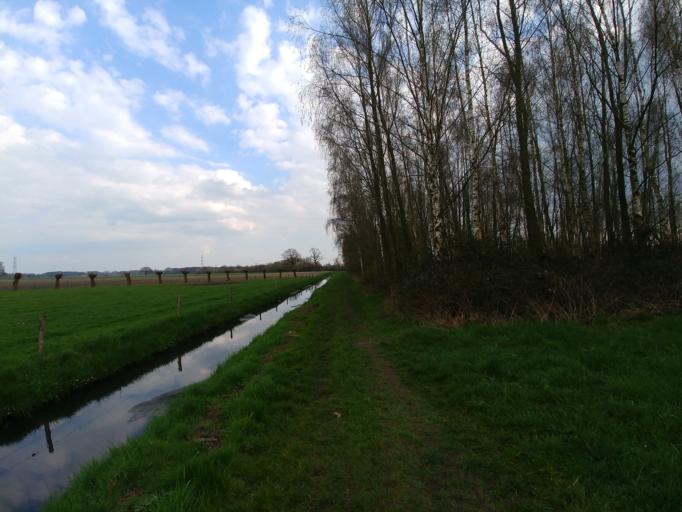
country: NL
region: Gelderland
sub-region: Gemeente Voorst
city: Twello
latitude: 52.2545
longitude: 6.0890
